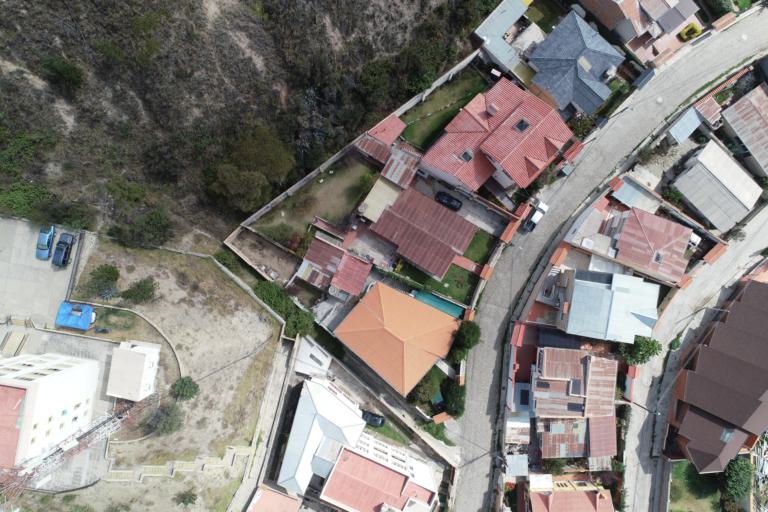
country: BO
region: La Paz
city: La Paz
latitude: -16.5209
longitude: -68.0910
